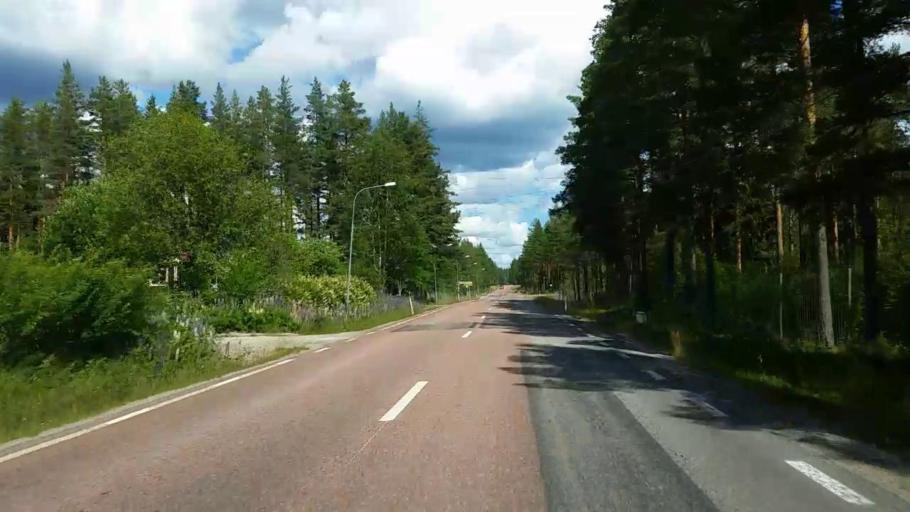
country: SE
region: Gaevleborg
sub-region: Ovanakers Kommun
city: Edsbyn
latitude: 61.3539
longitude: 15.6885
